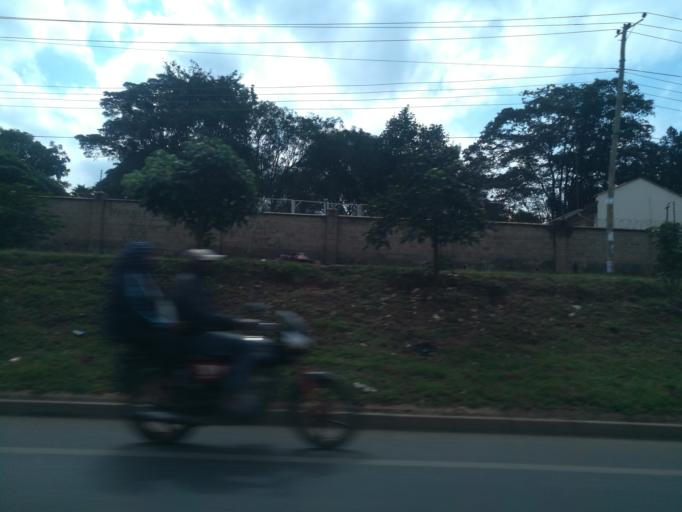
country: KE
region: Nairobi Area
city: Nairobi
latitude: -1.2808
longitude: 36.7892
